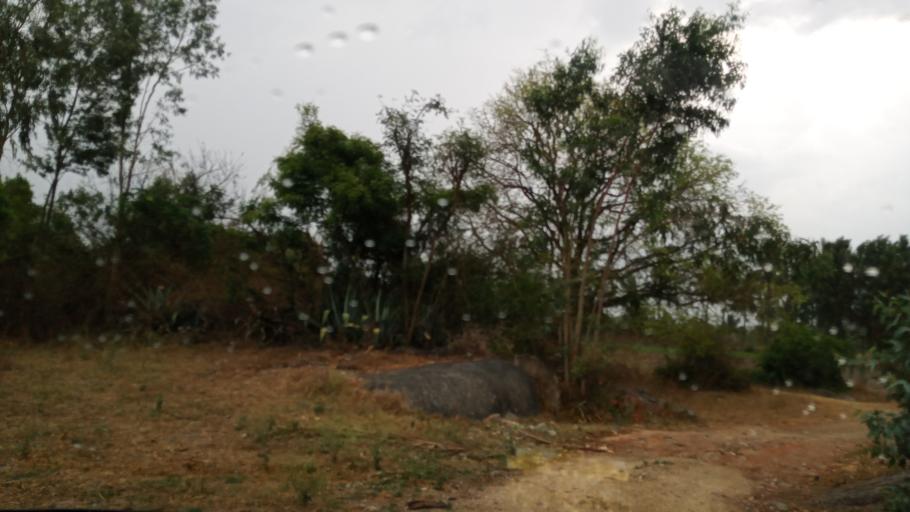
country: IN
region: Karnataka
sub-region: Kolar
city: Mulbagal
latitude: 13.1038
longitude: 78.3223
